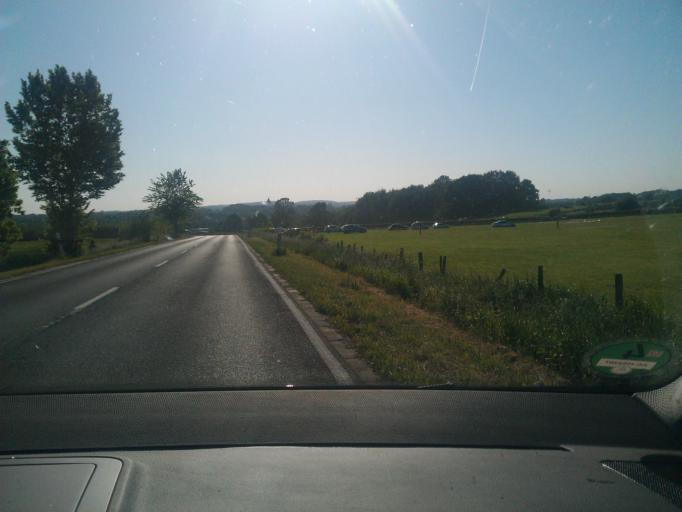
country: DE
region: North Rhine-Westphalia
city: Stolberg
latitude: 50.7283
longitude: 6.1975
